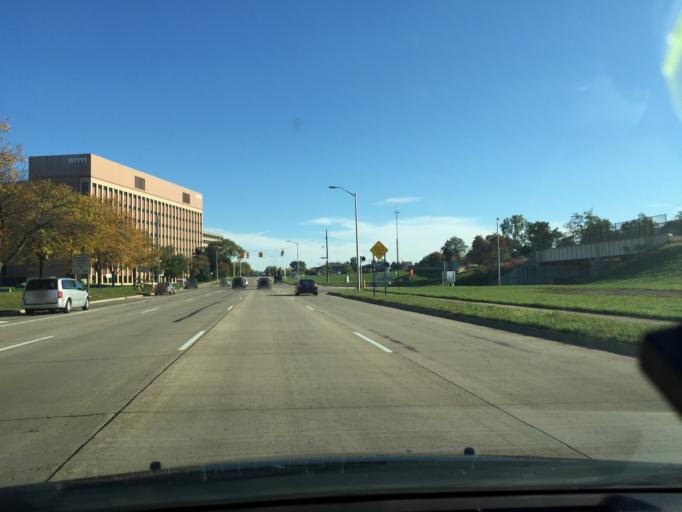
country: US
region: Michigan
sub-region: Oakland County
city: Pontiac
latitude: 42.6354
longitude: -83.2939
